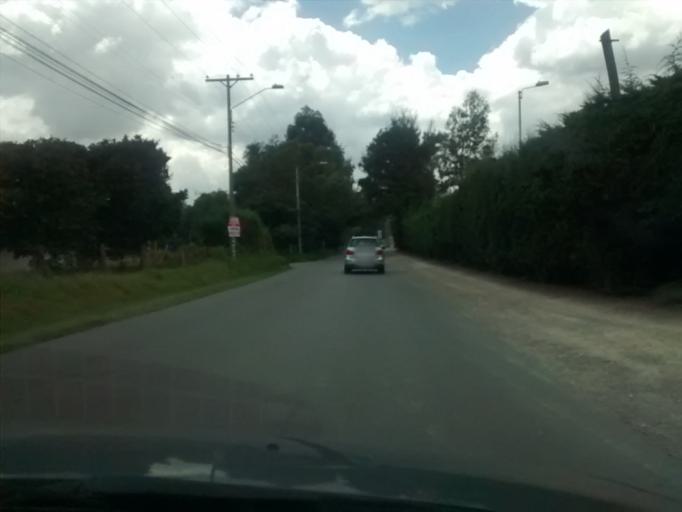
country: CO
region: Cundinamarca
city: Chia
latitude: 4.8096
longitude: -74.0381
